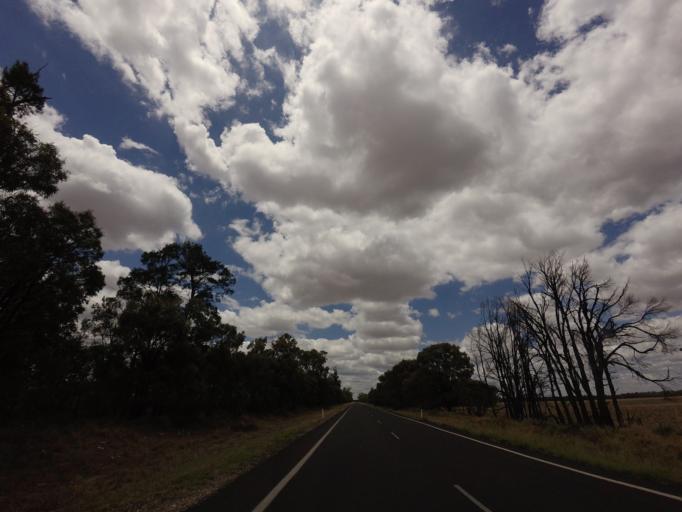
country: AU
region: Queensland
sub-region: Goondiwindi
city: Goondiwindi
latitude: -28.1473
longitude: 150.6851
